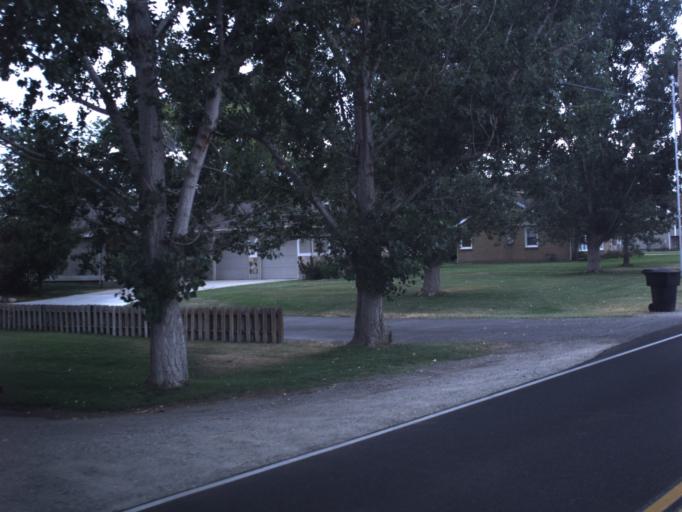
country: US
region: Utah
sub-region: Davis County
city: Syracuse
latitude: 41.0892
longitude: -112.0937
